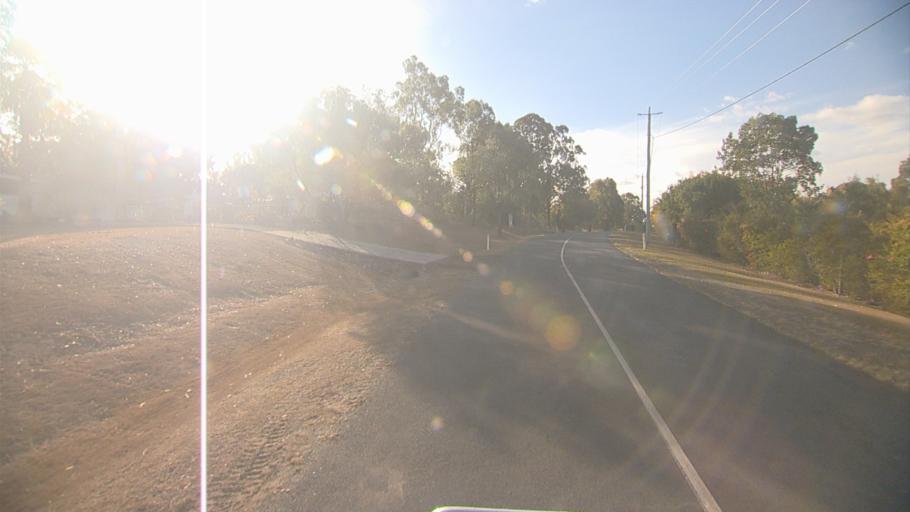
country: AU
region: Queensland
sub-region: Logan
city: Cedar Vale
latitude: -27.8793
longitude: 153.0104
